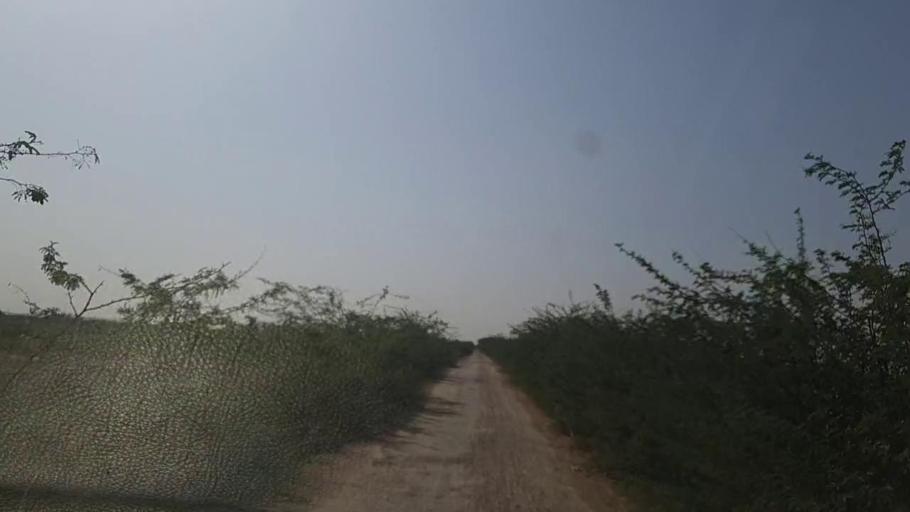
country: PK
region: Sindh
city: Kadhan
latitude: 24.5689
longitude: 69.2829
